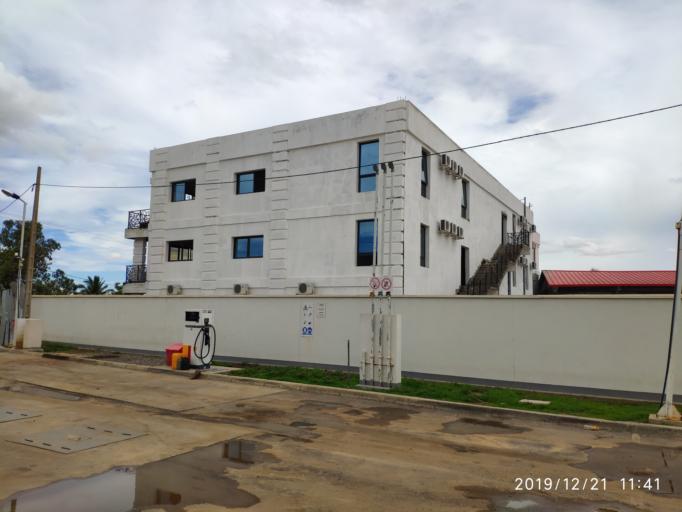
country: MG
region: Diana
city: Ambilobe
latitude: -13.1863
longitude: 49.0530
